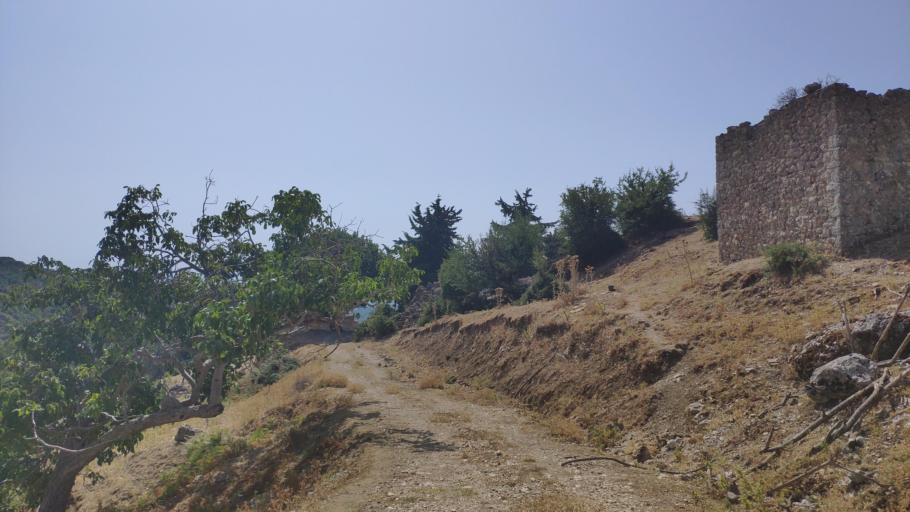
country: GR
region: West Greece
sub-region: Nomos Aitolias kai Akarnanias
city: Monastirakion
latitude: 38.8150
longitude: 21.0173
